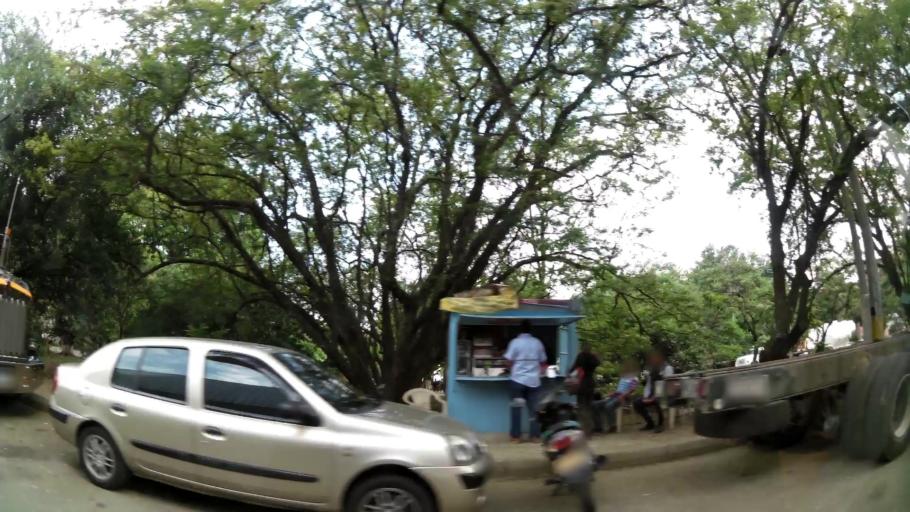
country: CO
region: Antioquia
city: Medellin
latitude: 6.2293
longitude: -75.5794
